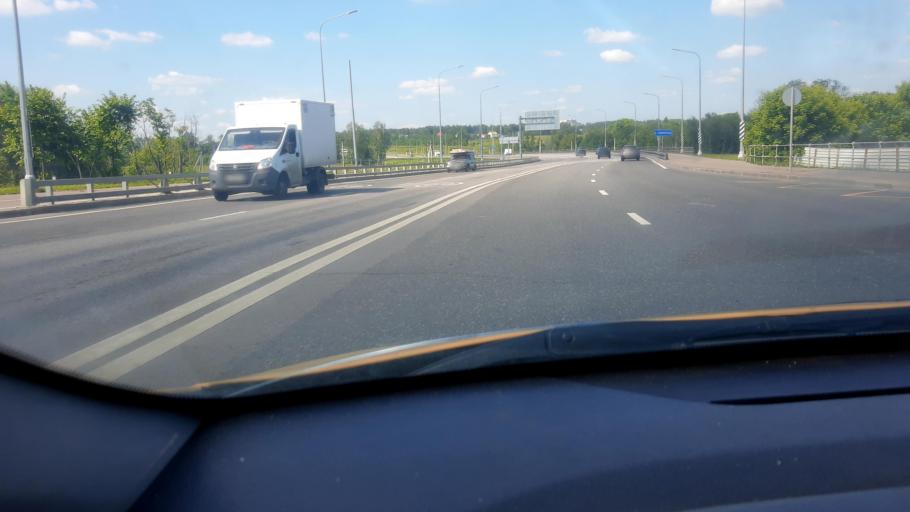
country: RU
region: Moskovskaya
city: Kokoshkino
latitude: 55.5803
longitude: 37.1632
